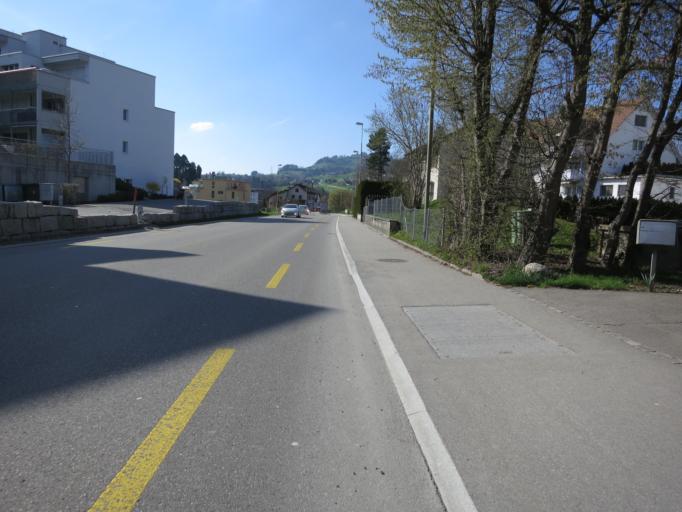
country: CH
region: Zurich
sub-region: Bezirk Hinwil
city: Wald
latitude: 47.2682
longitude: 8.9167
